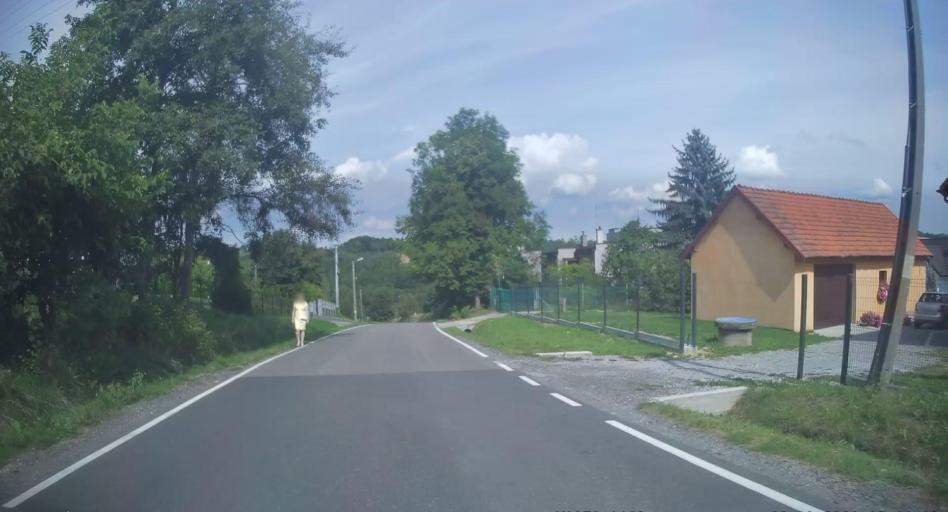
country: PL
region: Lesser Poland Voivodeship
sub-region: Powiat wielicki
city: Pawlikowice
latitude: 49.9484
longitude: 20.0407
